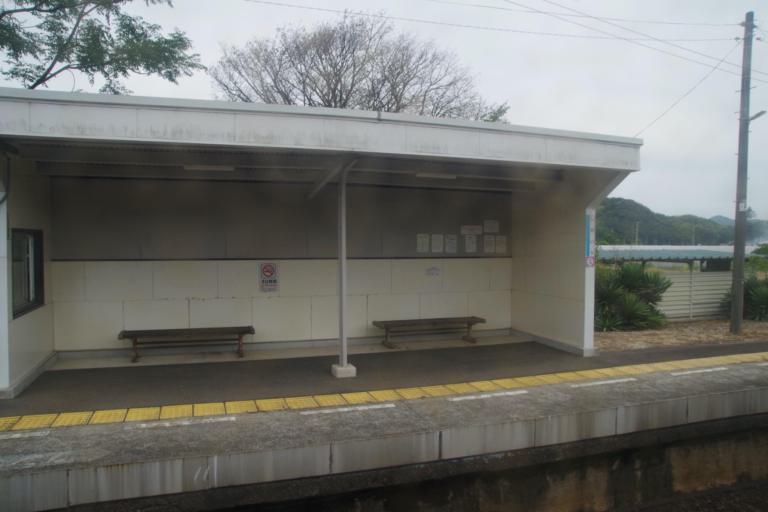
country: JP
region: Tokushima
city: Ikedacho
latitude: 34.1560
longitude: 133.8498
